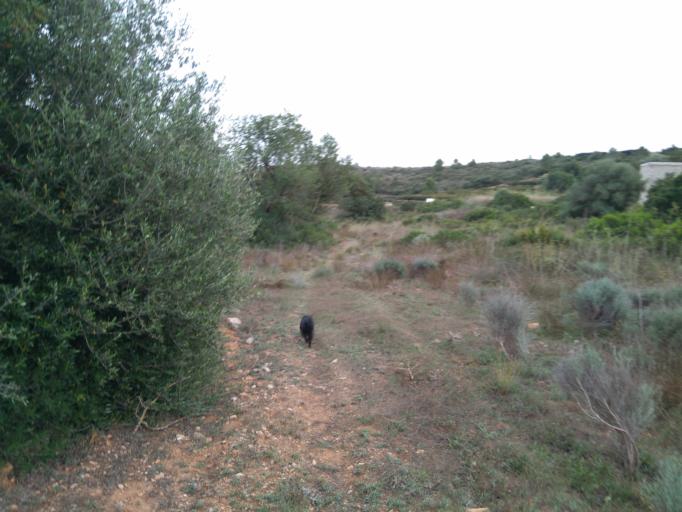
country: ES
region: Valencia
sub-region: Provincia de Valencia
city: Benimodo
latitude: 39.1990
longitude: -0.5876
